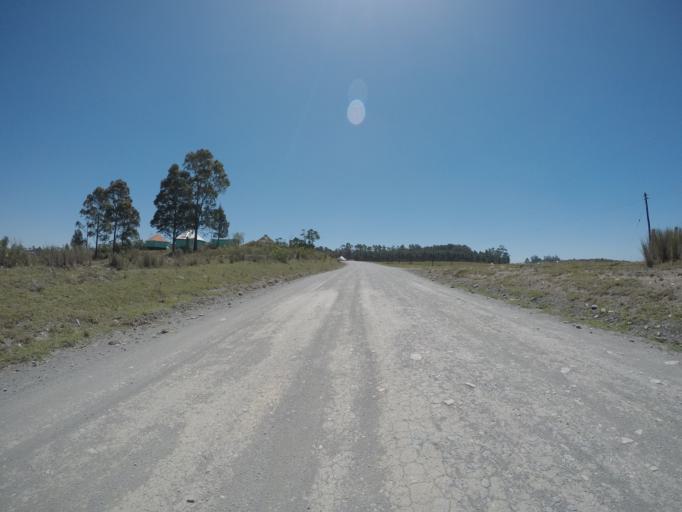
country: ZA
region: Eastern Cape
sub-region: OR Tambo District Municipality
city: Libode
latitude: -31.9643
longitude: 29.0250
